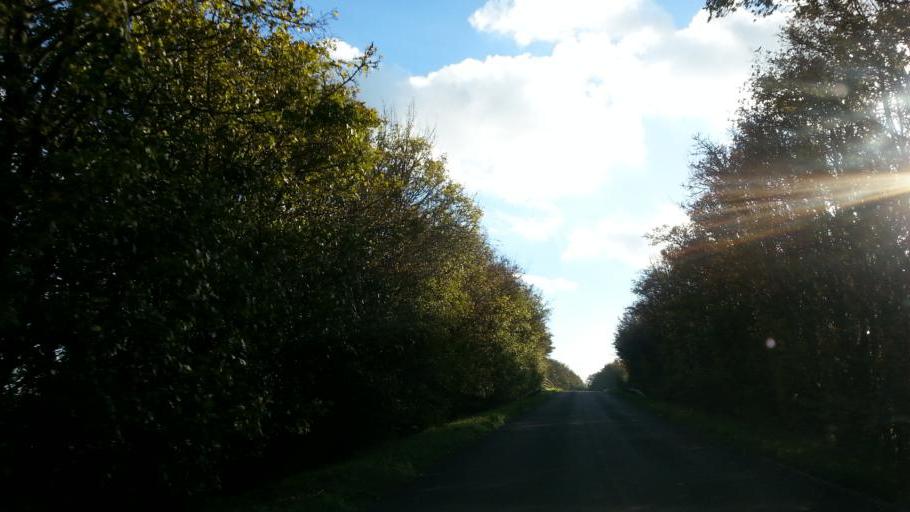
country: GB
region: England
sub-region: Suffolk
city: Thurston
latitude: 52.2375
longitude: 0.8081
